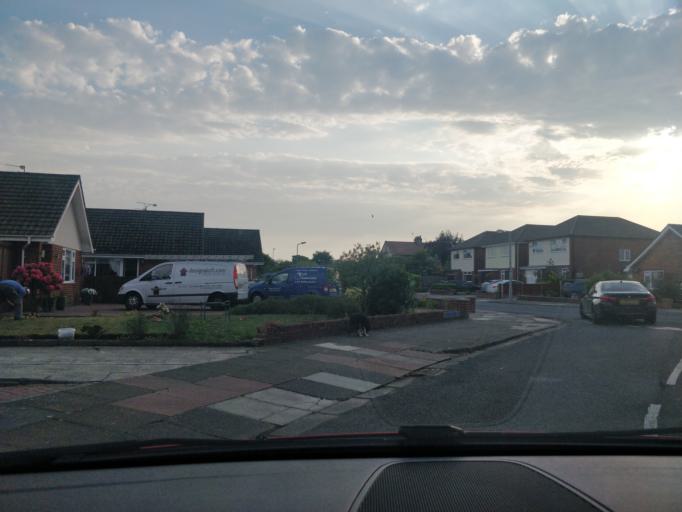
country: GB
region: England
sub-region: Sefton
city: Southport
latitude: 53.6709
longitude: -2.9719
